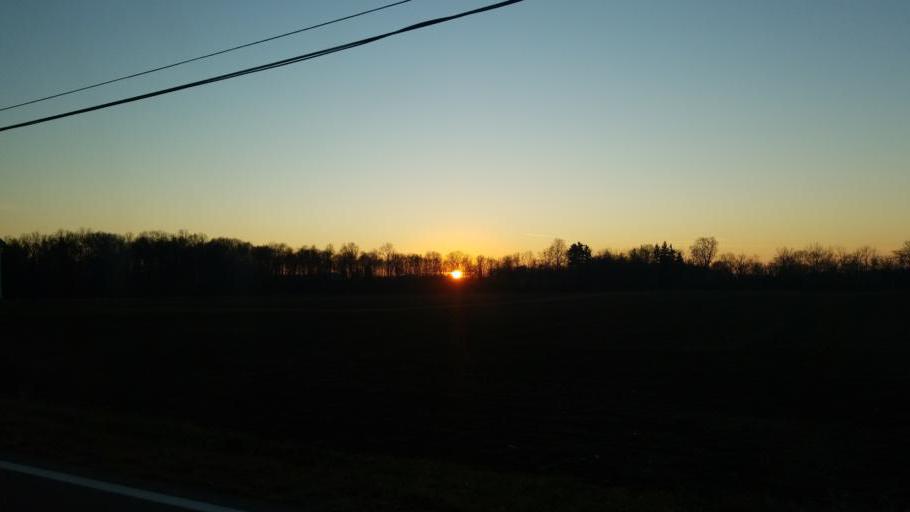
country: US
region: Ohio
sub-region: Wyandot County
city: Upper Sandusky
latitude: 40.8314
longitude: -83.1315
